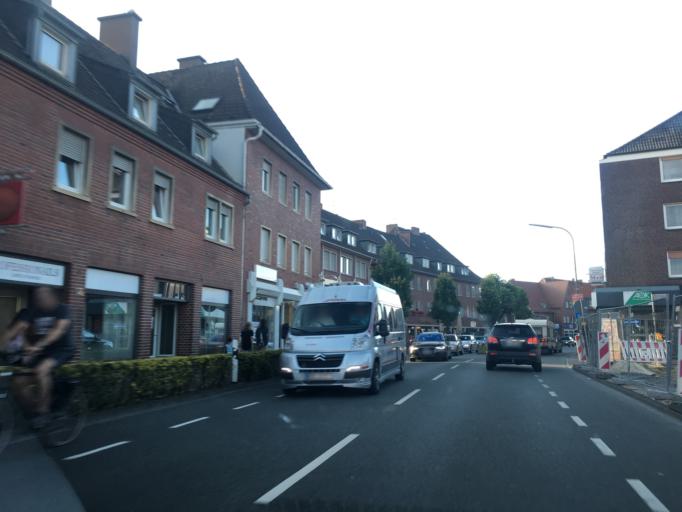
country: DE
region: North Rhine-Westphalia
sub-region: Regierungsbezirk Munster
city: Dulmen
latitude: 51.8293
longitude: 7.2793
